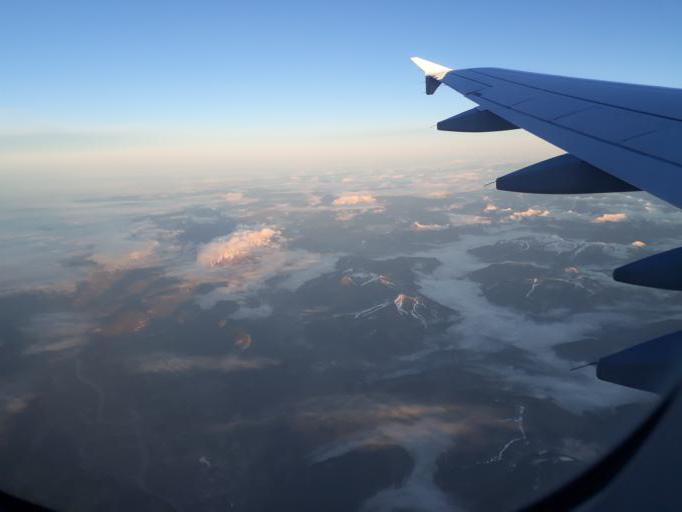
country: AT
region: Tyrol
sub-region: Politischer Bezirk Kufstein
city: Radfeld
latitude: 47.4412
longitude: 11.9391
